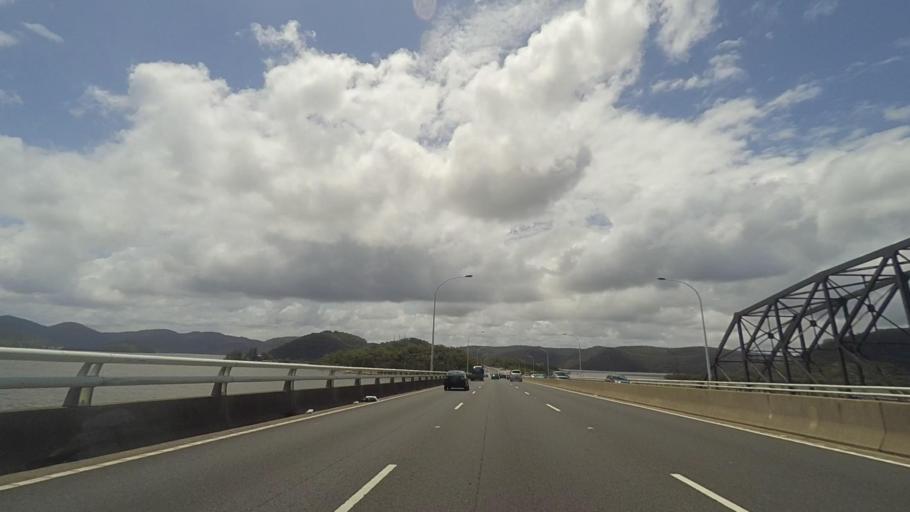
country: AU
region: New South Wales
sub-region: Hornsby Shire
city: Berowra
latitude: -33.5396
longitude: 151.1985
